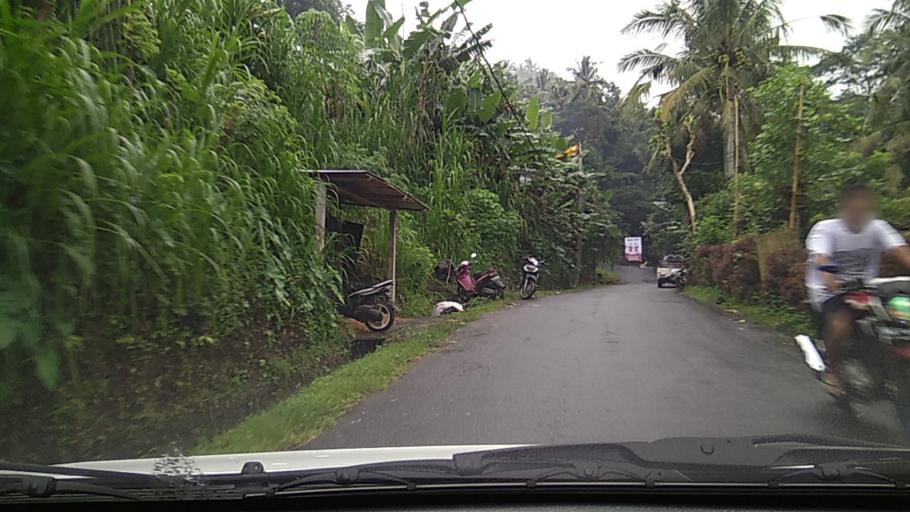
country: ID
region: Bali
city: Tiyingtali Kelod
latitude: -8.3934
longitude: 115.6209
